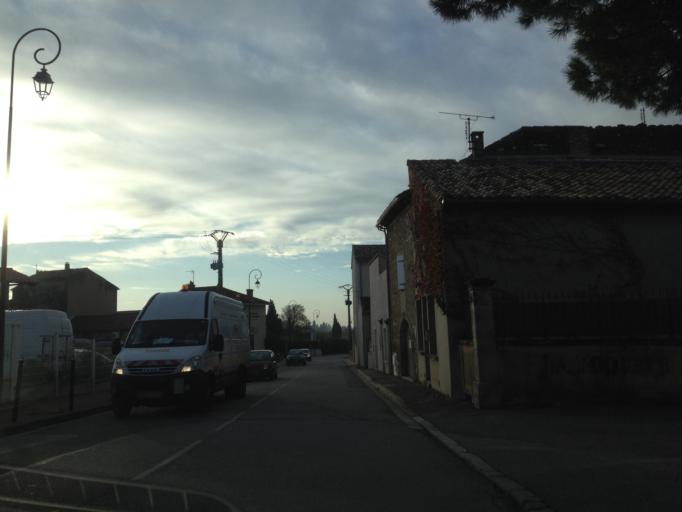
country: FR
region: Provence-Alpes-Cote d'Azur
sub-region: Departement du Vaucluse
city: Chateauneuf-du-Pape
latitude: 44.0582
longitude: 4.8346
